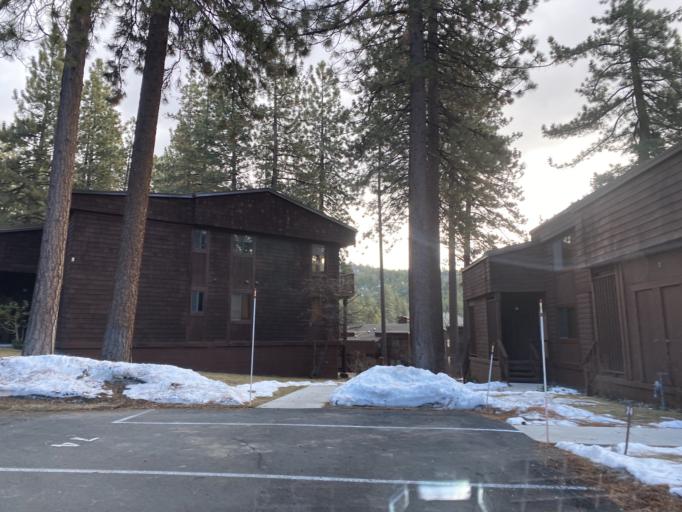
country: US
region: Nevada
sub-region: Douglas County
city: Kingsbury
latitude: 38.9959
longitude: -119.9539
